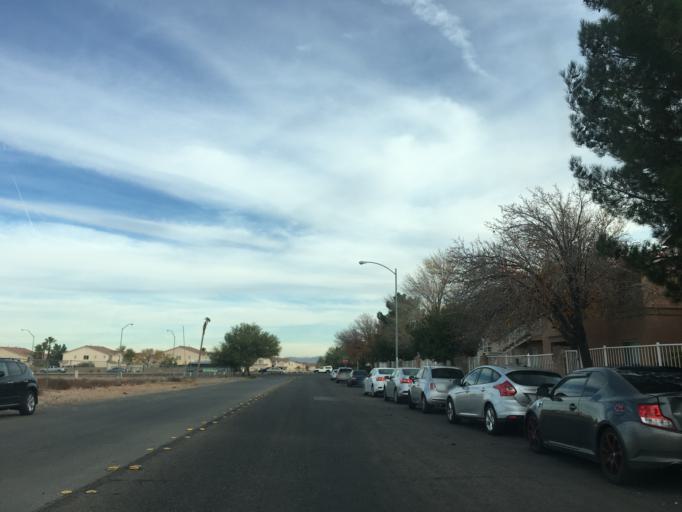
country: US
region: Nevada
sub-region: Clark County
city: Enterprise
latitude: 36.0155
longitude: -115.1740
